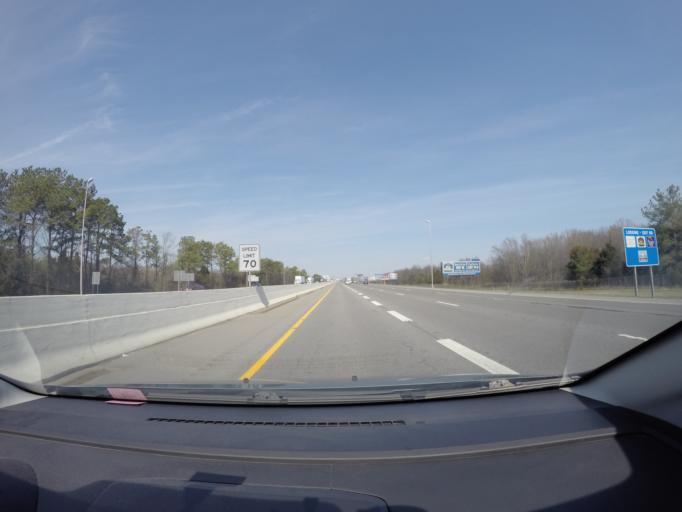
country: US
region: Tennessee
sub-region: Rutherford County
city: Murfreesboro
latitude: 35.8195
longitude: -86.4046
